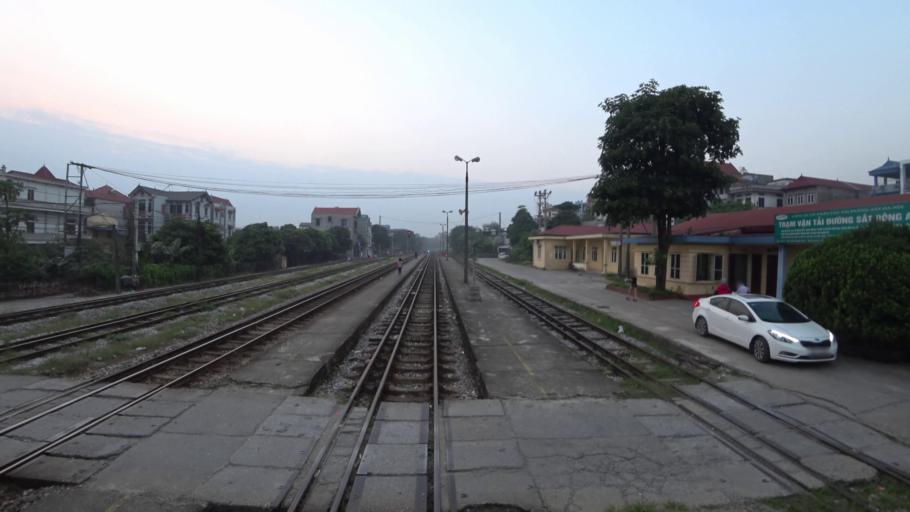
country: VN
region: Ha Noi
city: Dong Anh
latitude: 21.1783
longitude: 105.8525
